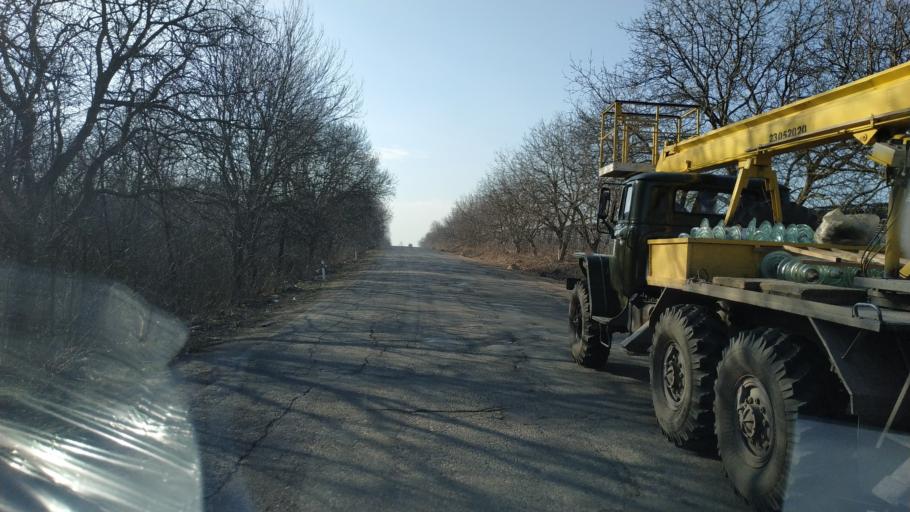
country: MD
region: Chisinau
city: Singera
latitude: 46.8621
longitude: 29.0317
